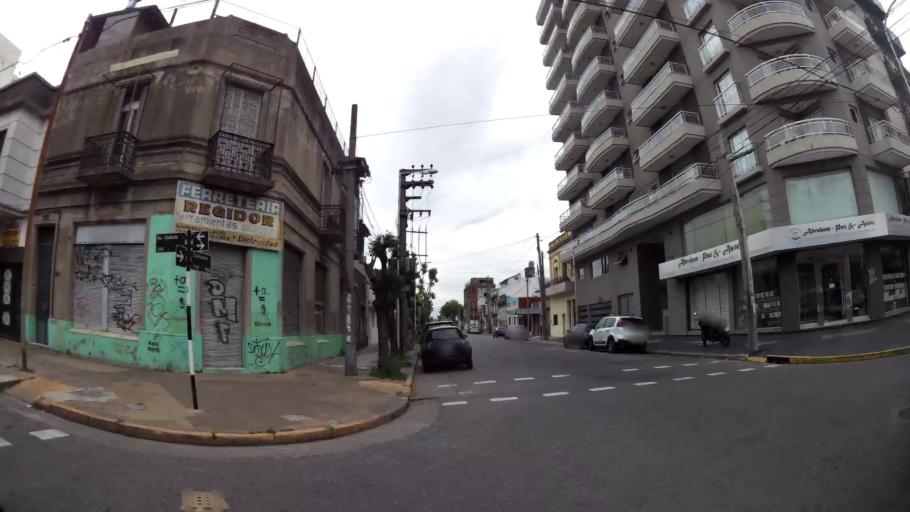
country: AR
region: Buenos Aires
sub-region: Partido de Avellaneda
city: Avellaneda
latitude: -34.6747
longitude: -58.3857
